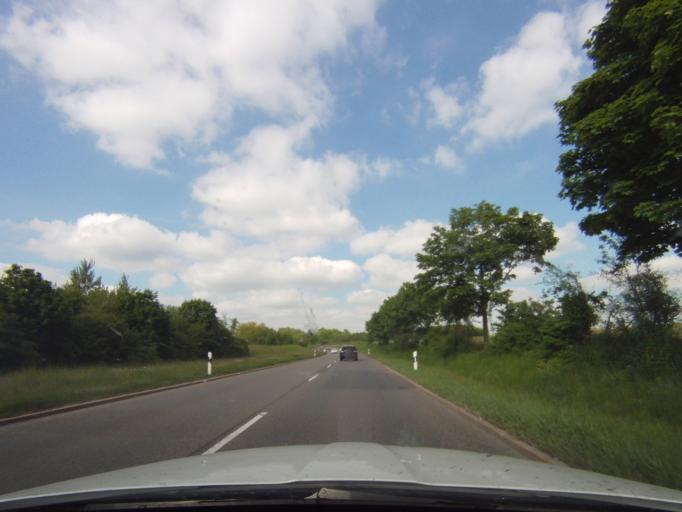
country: DE
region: Thuringia
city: Gera
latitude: 50.8712
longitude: 12.1157
